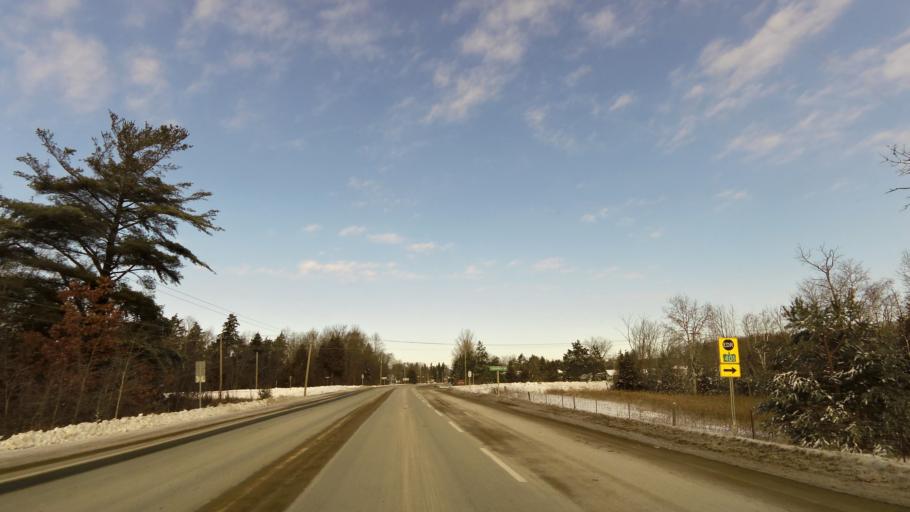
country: CA
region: Ontario
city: Quinte West
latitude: 44.1259
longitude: -77.7845
